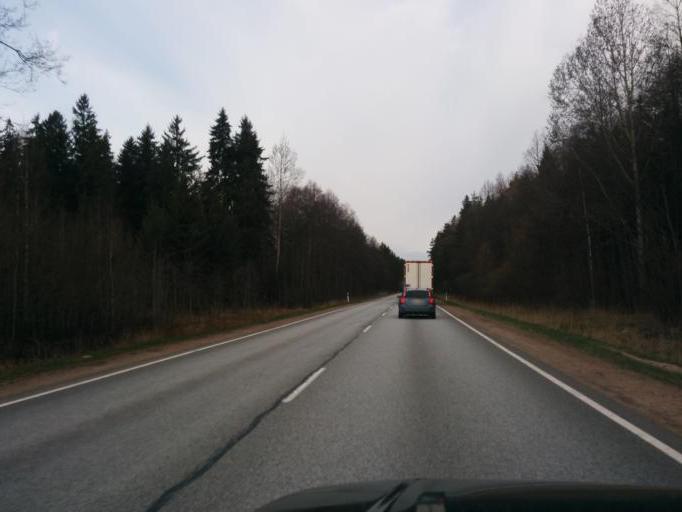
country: LV
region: Kekava
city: Balozi
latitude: 56.8252
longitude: 24.0659
